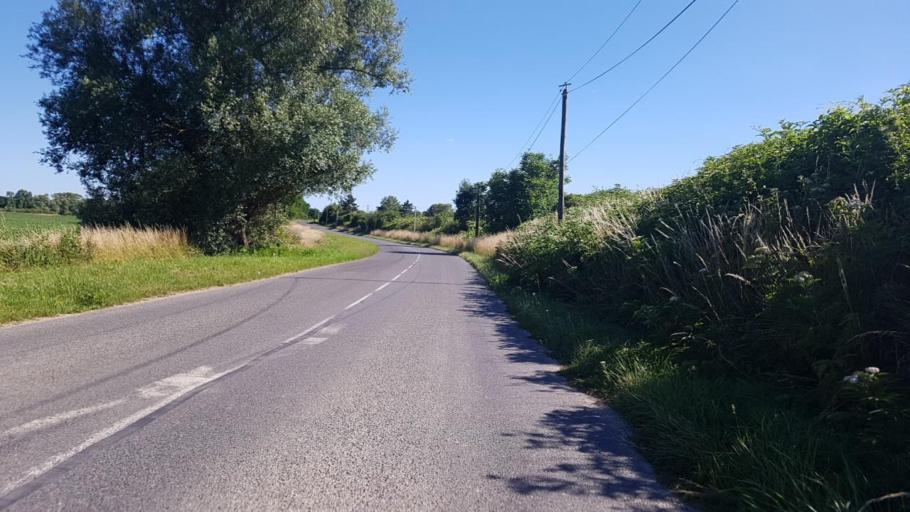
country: FR
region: Ile-de-France
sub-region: Departement de Seine-et-Marne
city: Esbly
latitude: 48.9406
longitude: 2.7992
